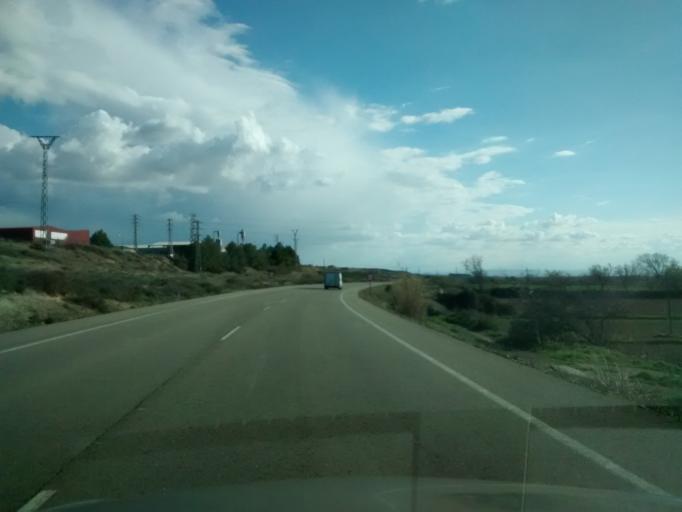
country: ES
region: Aragon
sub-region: Provincia de Zaragoza
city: San Mateo de Gallego
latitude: 41.8182
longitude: -0.7749
